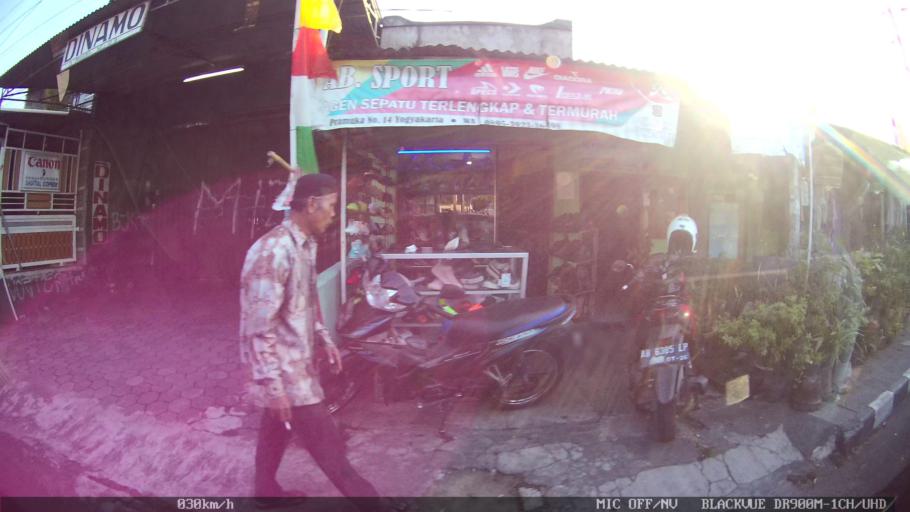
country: ID
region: Daerah Istimewa Yogyakarta
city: Yogyakarta
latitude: -7.8178
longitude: 110.3870
